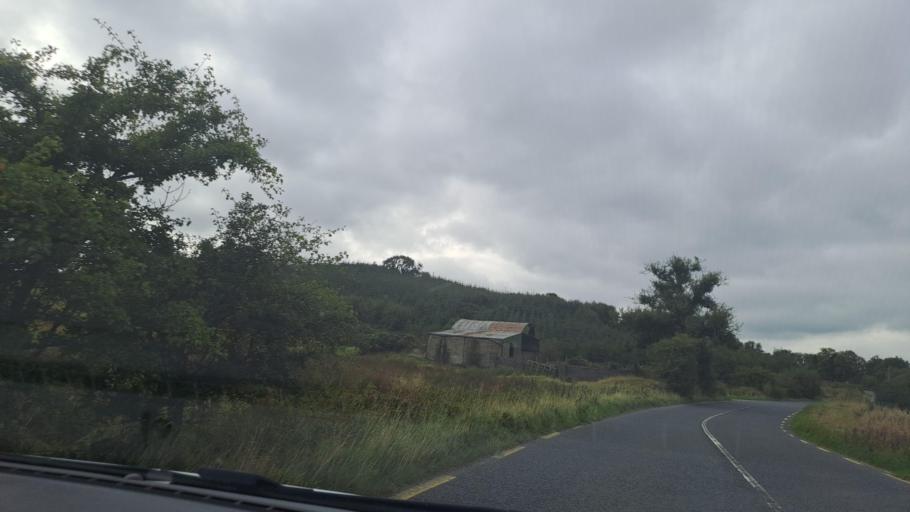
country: IE
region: Ulster
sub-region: An Cabhan
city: Bailieborough
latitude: 53.9280
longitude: -6.9306
